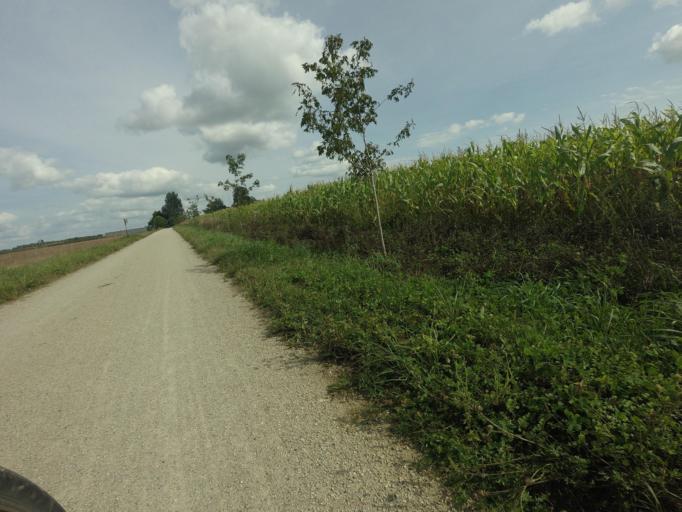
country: CA
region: Ontario
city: Waterloo
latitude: 43.6015
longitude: -80.5309
